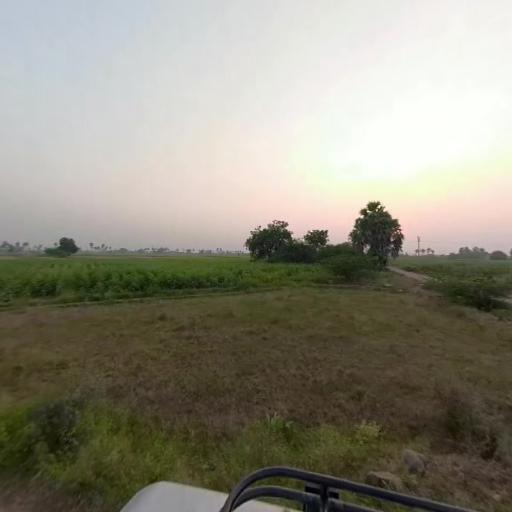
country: IN
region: Telangana
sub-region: Nalgonda
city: Suriapet
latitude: 17.0780
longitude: 79.5495
